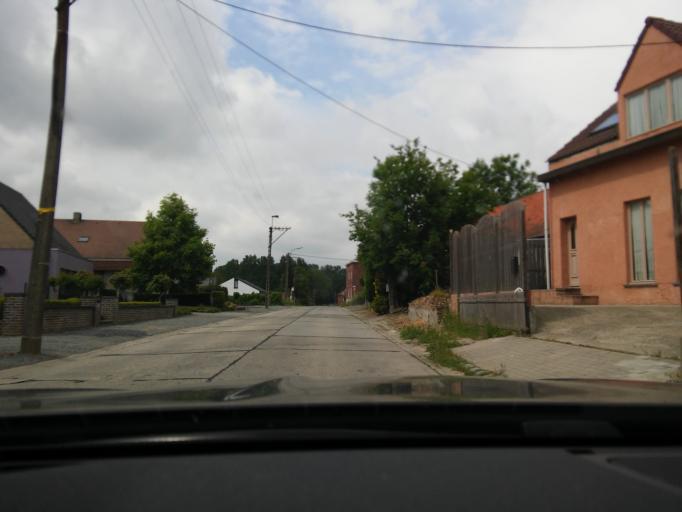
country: BE
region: Flanders
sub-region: Provincie Oost-Vlaanderen
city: Ninove
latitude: 50.7951
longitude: 4.0086
